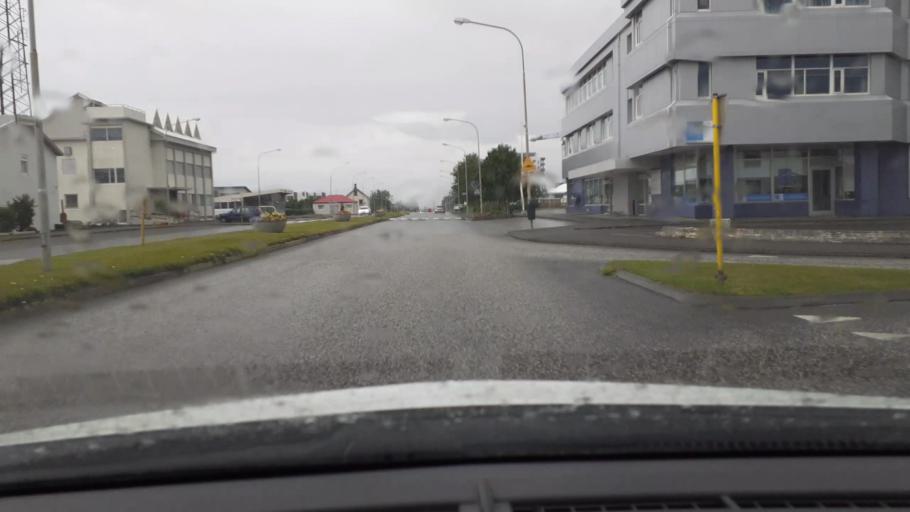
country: IS
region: West
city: Akranes
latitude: 64.3195
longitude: -22.0790
